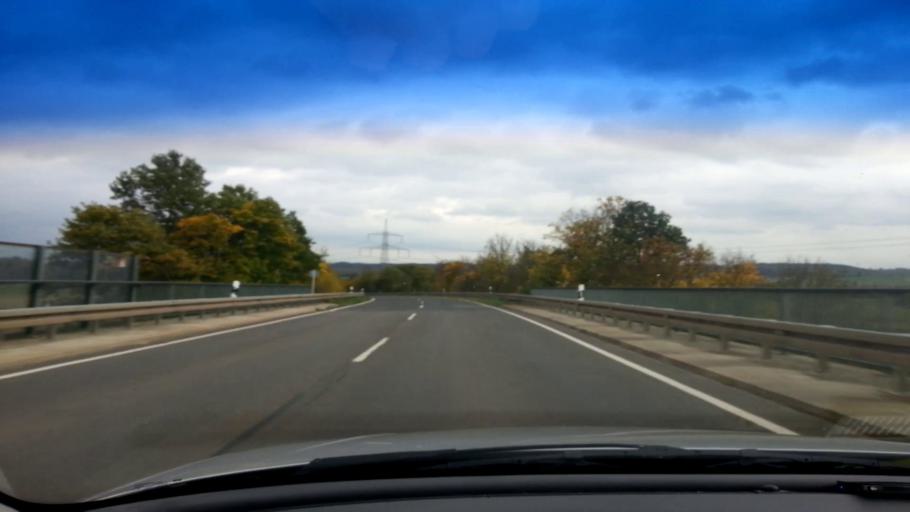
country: DE
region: Bavaria
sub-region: Upper Franconia
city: Viereth-Trunstadt
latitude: 49.9413
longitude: 10.7613
